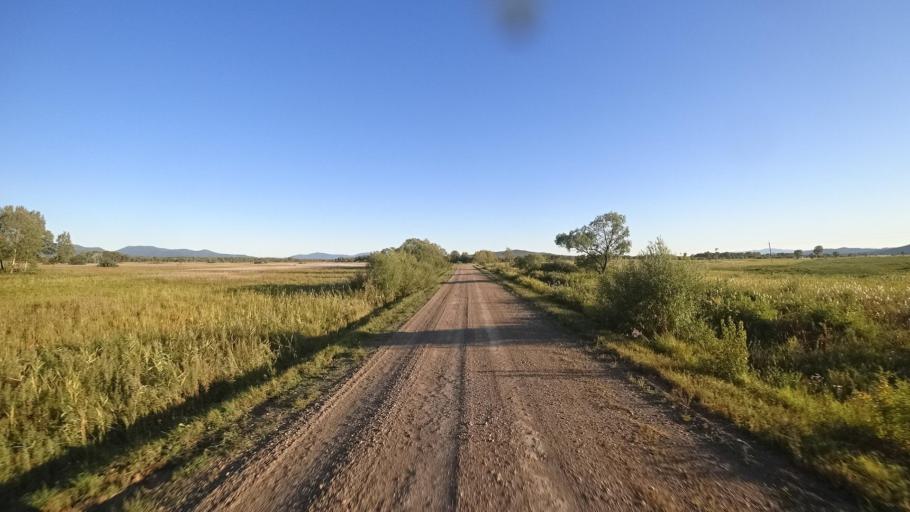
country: RU
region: Primorskiy
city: Kirovskiy
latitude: 44.7917
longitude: 133.6226
